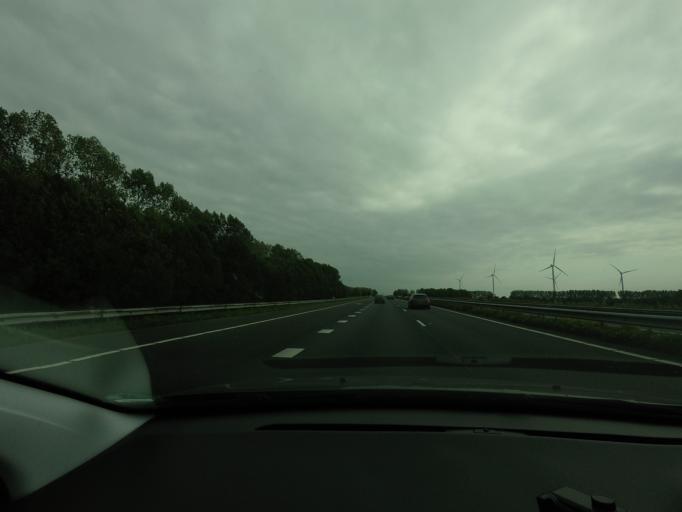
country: NL
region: North Brabant
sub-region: Gemeente Geertruidenberg
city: Geertruidenberg
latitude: 51.6817
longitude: 4.8526
